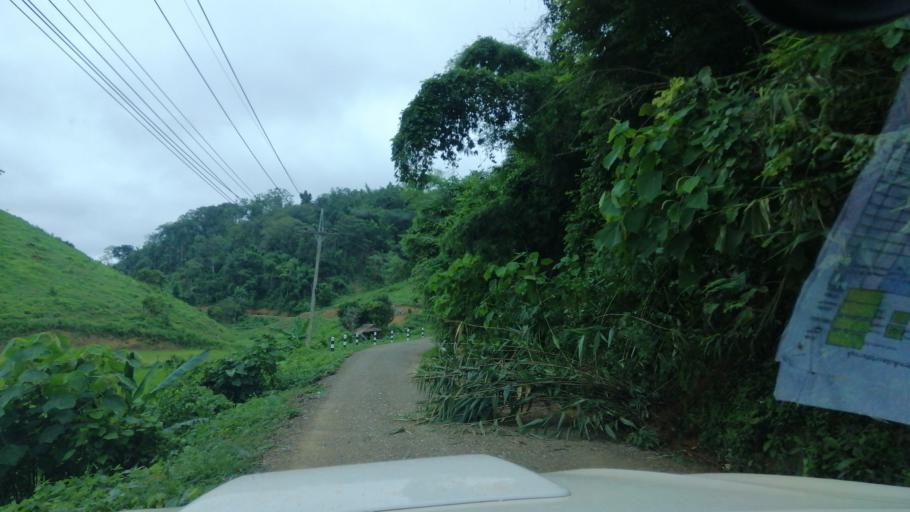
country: LA
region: Xiagnabouli
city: Muang Kenthao
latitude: 17.9322
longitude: 101.3885
